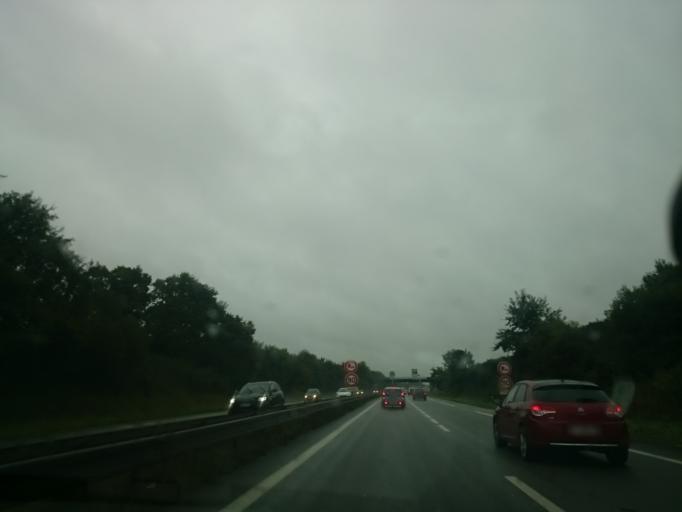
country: FR
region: Brittany
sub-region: Departement du Morbihan
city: Vannes
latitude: 47.6689
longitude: -2.7379
